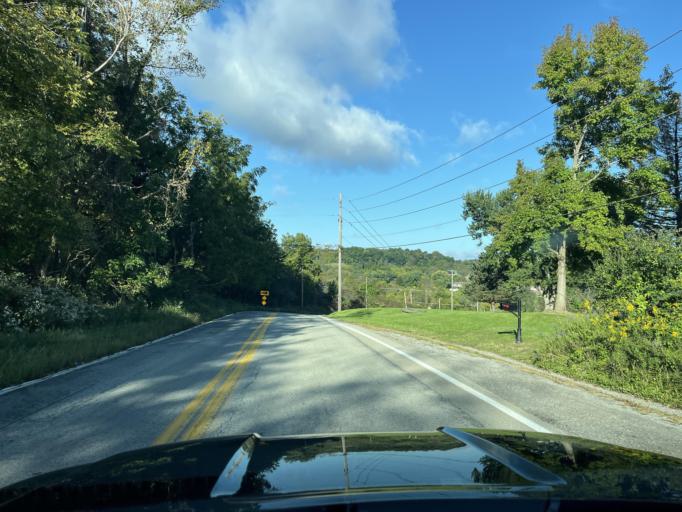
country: US
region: Pennsylvania
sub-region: Fayette County
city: South Uniontown
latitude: 39.8820
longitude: -79.7490
